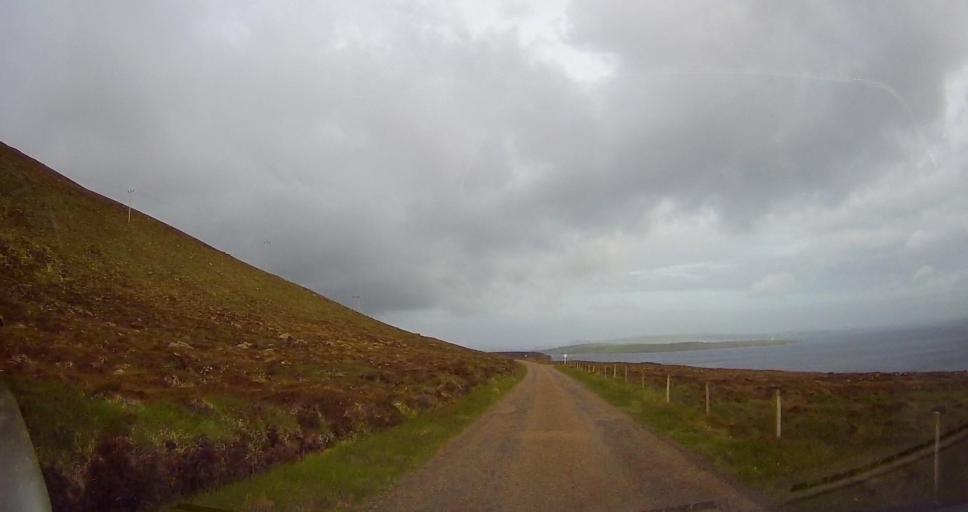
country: GB
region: Scotland
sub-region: Orkney Islands
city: Stromness
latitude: 58.8874
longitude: -3.2528
